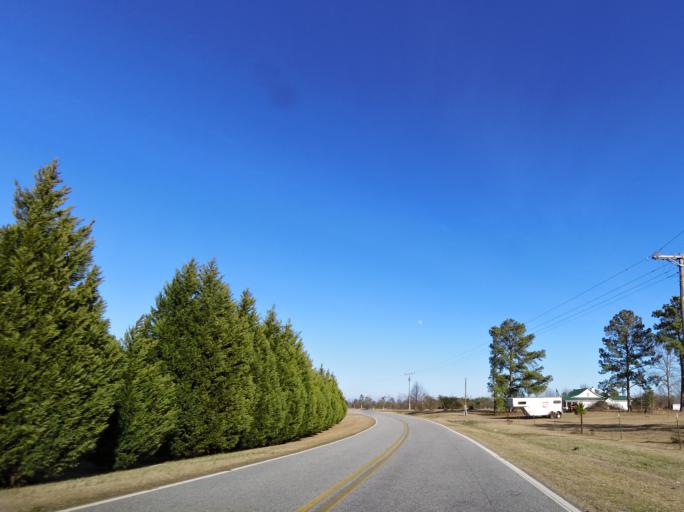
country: US
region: Georgia
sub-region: Bibb County
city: West Point
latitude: 32.7561
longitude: -83.8858
